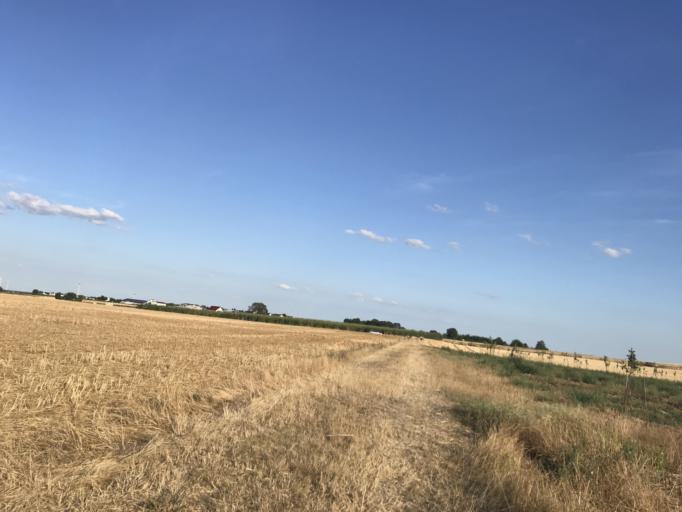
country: DE
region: Rheinland-Pfalz
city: Ober-Olm
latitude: 49.9469
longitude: 8.1786
